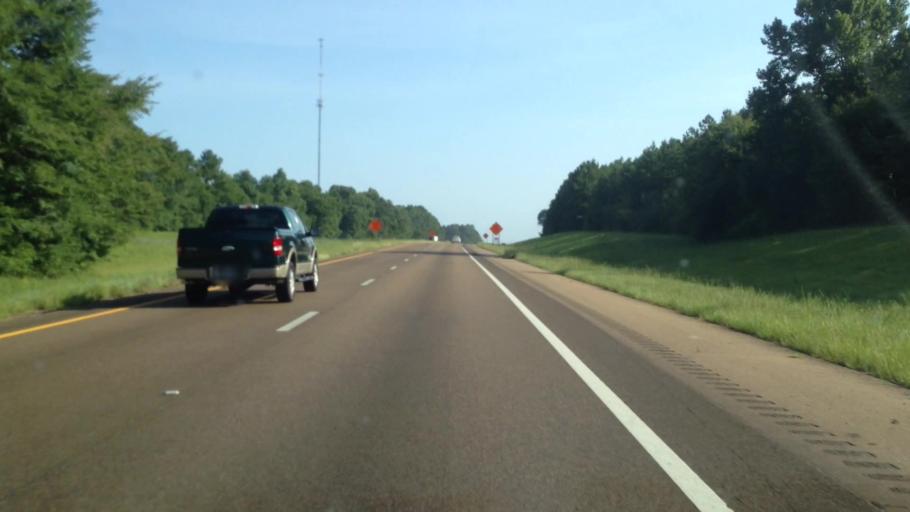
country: US
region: Mississippi
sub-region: Pike County
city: Summit
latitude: 31.4148
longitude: -90.4793
